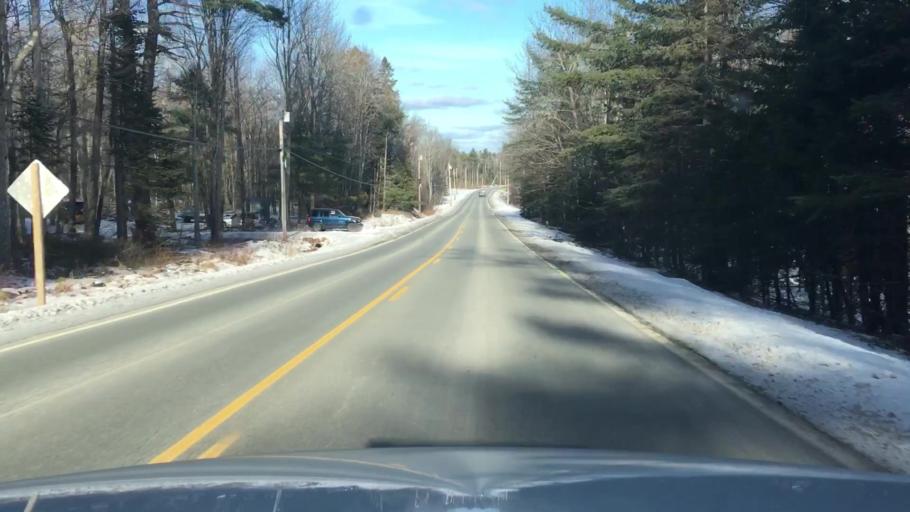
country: US
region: Maine
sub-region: Penobscot County
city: Holden
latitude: 44.7470
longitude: -68.6141
